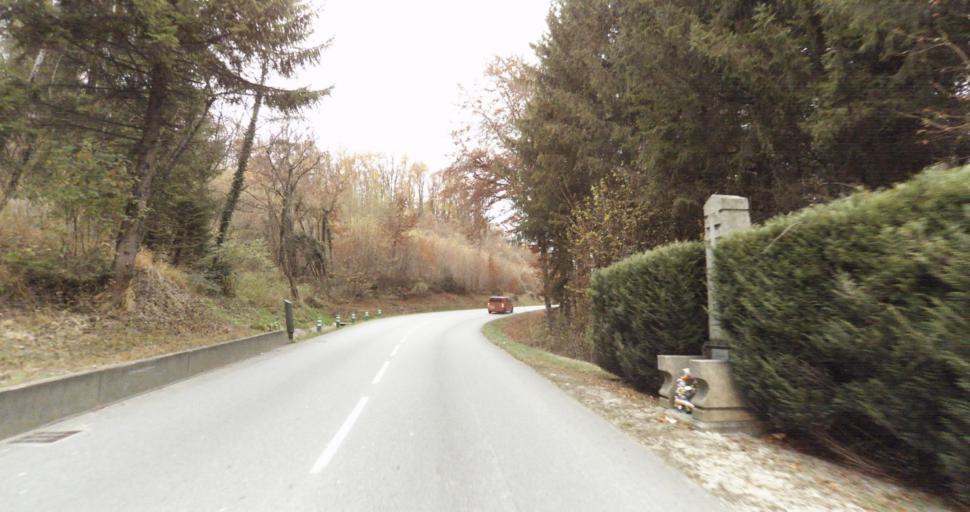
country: FR
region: Rhone-Alpes
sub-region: Departement de la Haute-Savoie
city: Chavanod
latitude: 45.8783
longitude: 6.0328
